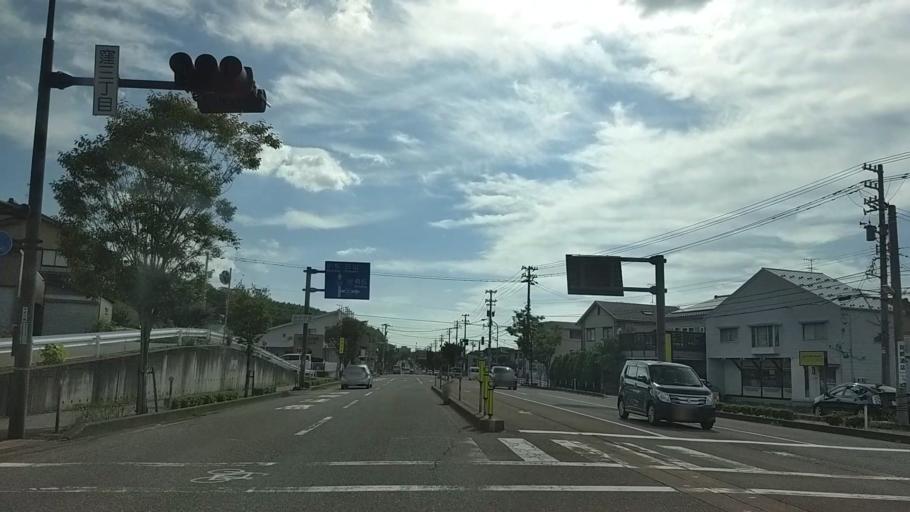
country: JP
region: Ishikawa
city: Nonoichi
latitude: 36.5240
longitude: 136.6424
